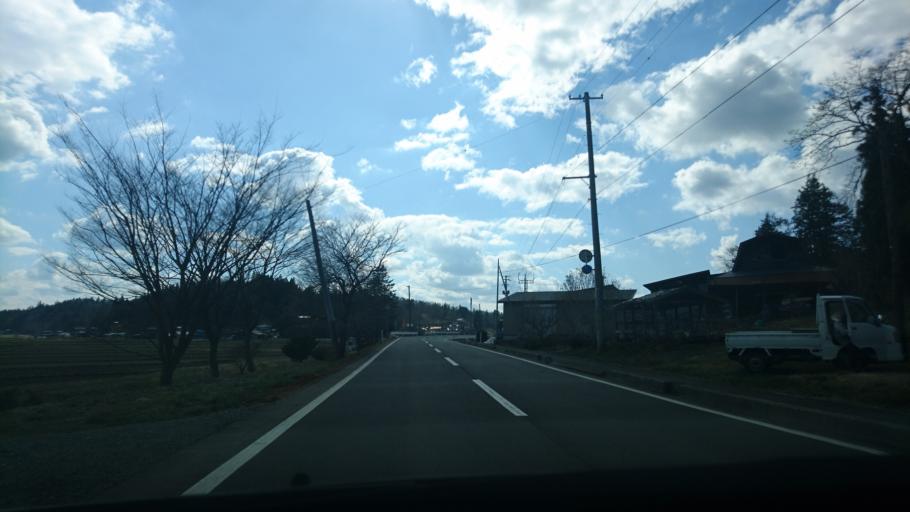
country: JP
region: Iwate
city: Kitakami
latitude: 39.3237
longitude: 141.2219
